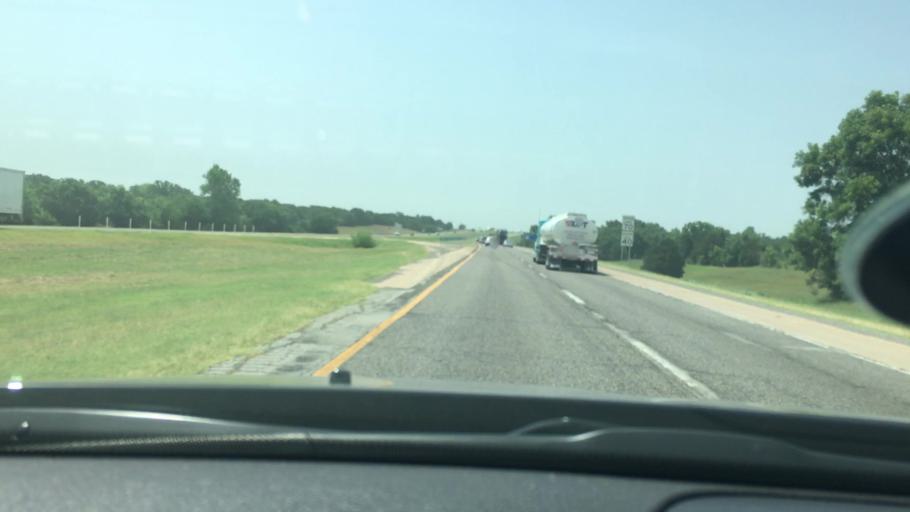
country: US
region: Oklahoma
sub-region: Garvin County
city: Wynnewood
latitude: 34.6408
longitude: -97.2192
